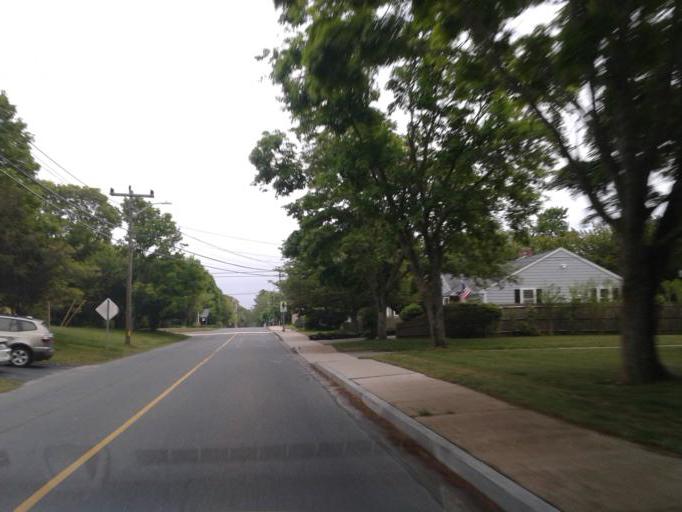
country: US
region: Massachusetts
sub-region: Barnstable County
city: Teaticket
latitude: 41.5698
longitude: -70.5900
